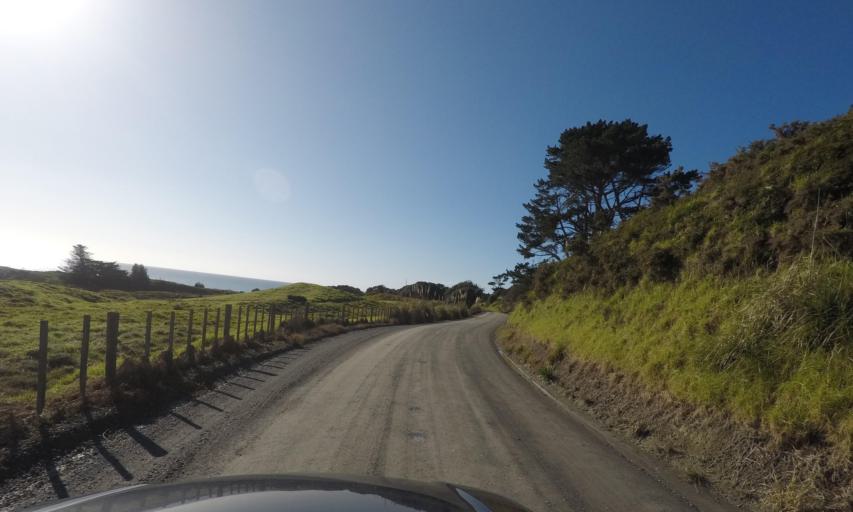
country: NZ
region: Auckland
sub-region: Auckland
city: Wellsford
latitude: -36.1605
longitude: 174.6438
